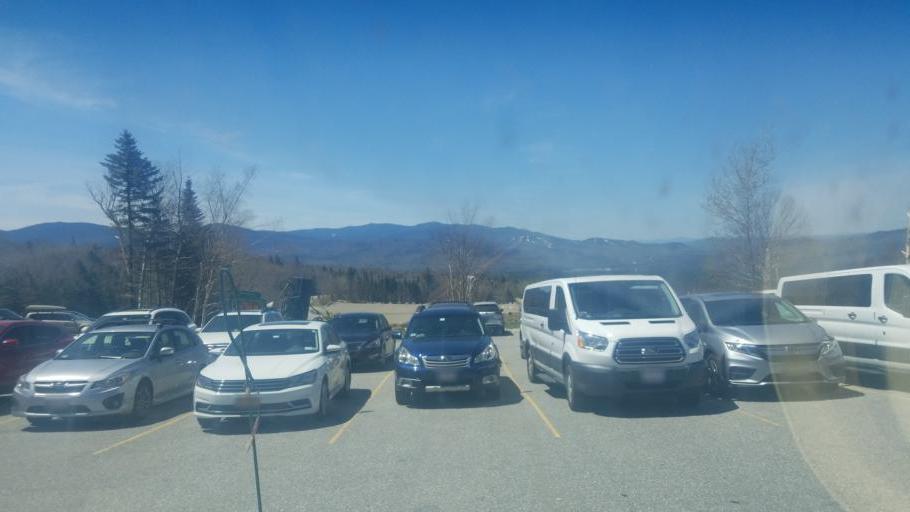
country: US
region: New Hampshire
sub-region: Coos County
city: Jefferson
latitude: 44.2696
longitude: -71.3509
